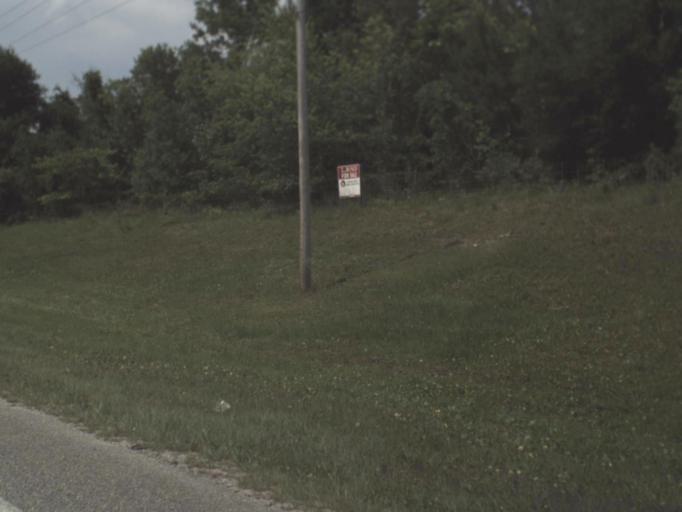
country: US
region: Florida
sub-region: Clay County
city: Green Cove Springs
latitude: 29.9186
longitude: -81.6817
